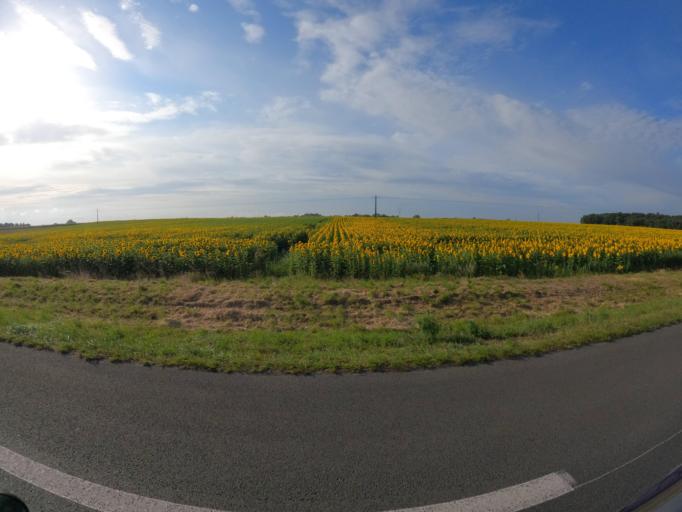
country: FR
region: Pays de la Loire
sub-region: Departement de Maine-et-Loire
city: Vaudelnay
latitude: 47.2088
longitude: -0.1879
